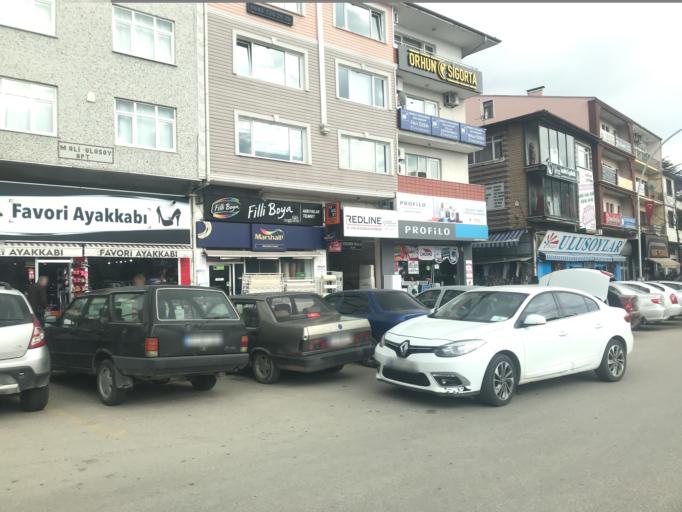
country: TR
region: Karabuk
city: Safranbolu
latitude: 41.2506
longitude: 32.6820
